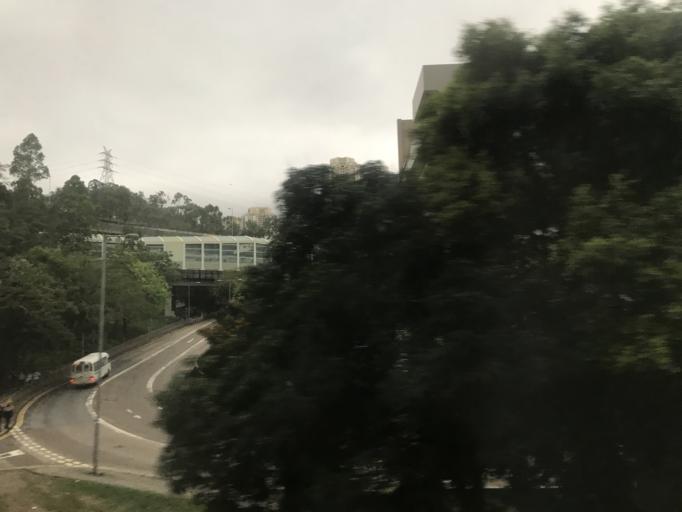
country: HK
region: Sha Tin
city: Sha Tin
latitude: 22.3713
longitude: 114.1759
